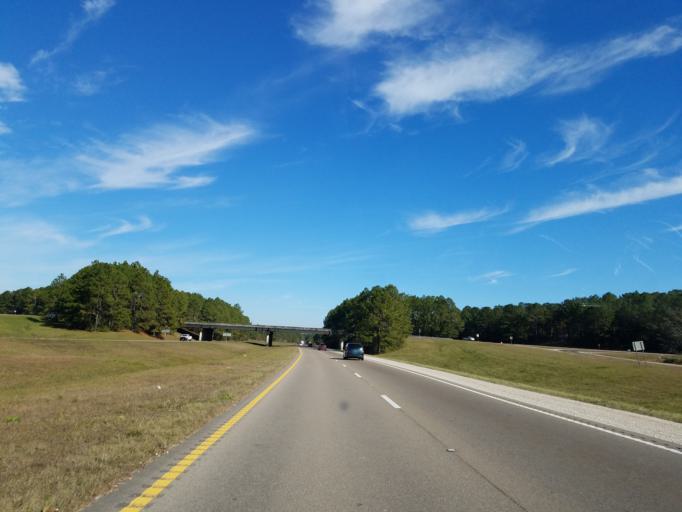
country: US
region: Mississippi
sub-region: Forrest County
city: Hattiesburg
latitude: 31.2390
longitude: -89.3042
